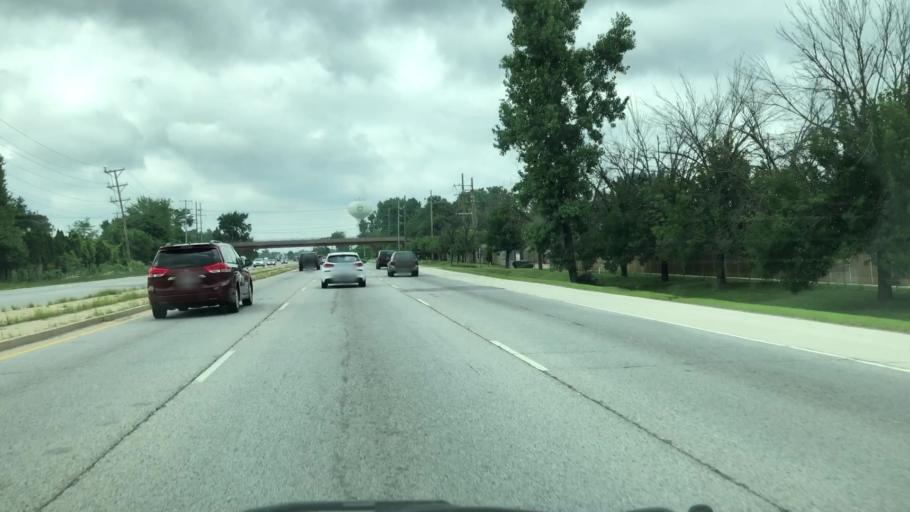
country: US
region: Illinois
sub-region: DuPage County
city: Elmhurst
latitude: 41.8842
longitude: -87.9614
